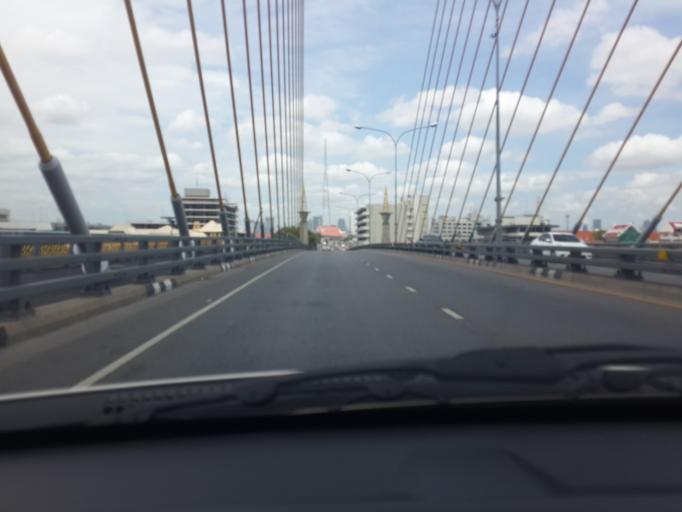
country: TH
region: Bangkok
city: Phra Nakhon
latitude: 13.7691
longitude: 100.4970
